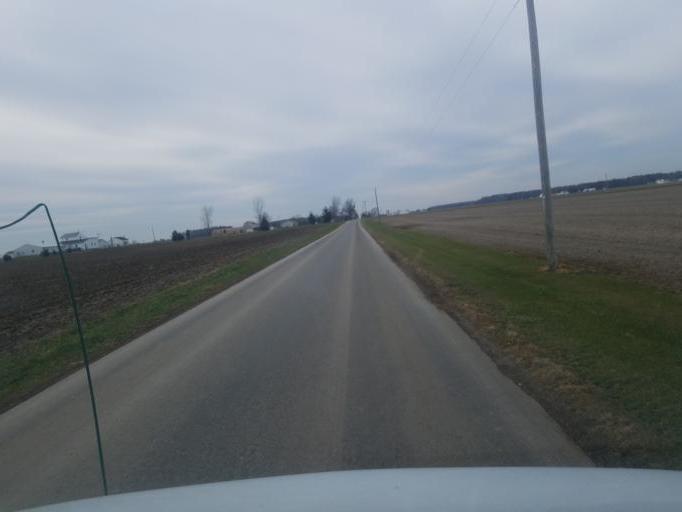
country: US
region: Indiana
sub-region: Adams County
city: Geneva
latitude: 40.6151
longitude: -84.8658
